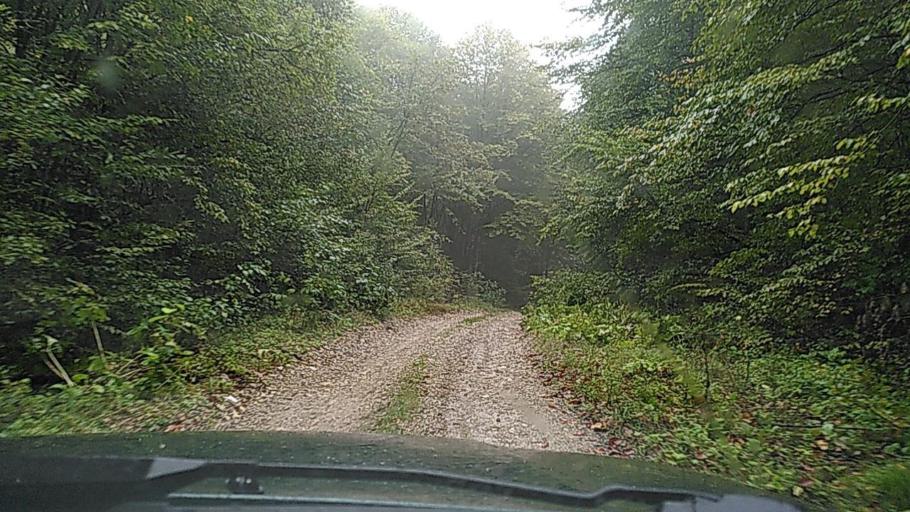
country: RU
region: Kabardino-Balkariya
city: Belaya Rechka
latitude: 43.3757
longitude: 43.4302
